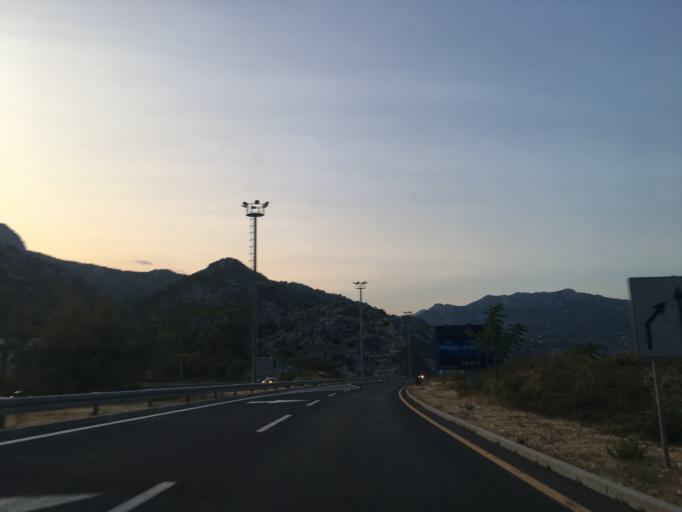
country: ME
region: Bar
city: Sutomore
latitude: 42.2021
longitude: 19.0511
